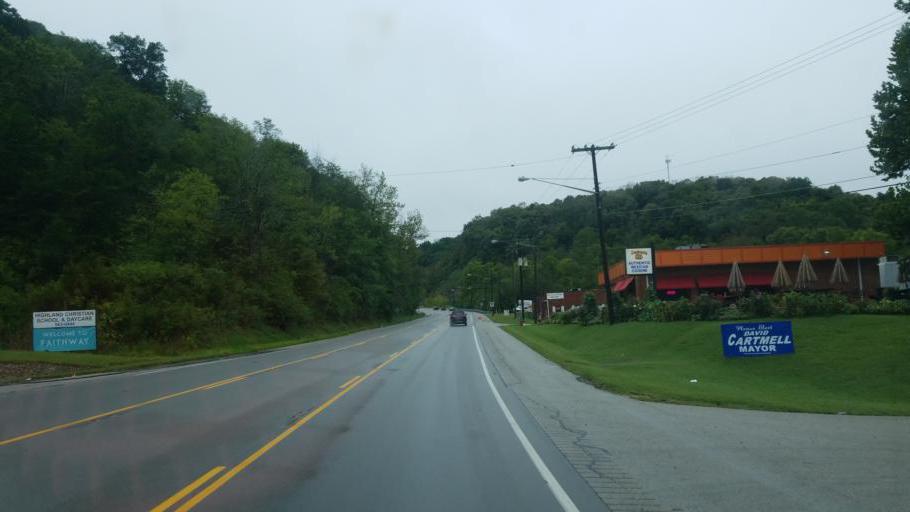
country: US
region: Kentucky
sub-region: Mason County
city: Maysville
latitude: 38.6386
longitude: -83.7595
